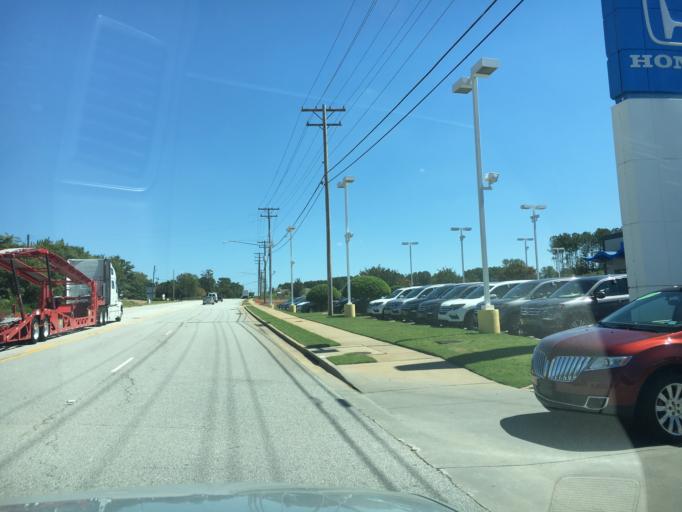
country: US
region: South Carolina
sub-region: Greenville County
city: Greenville
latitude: 34.8328
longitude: -82.3426
